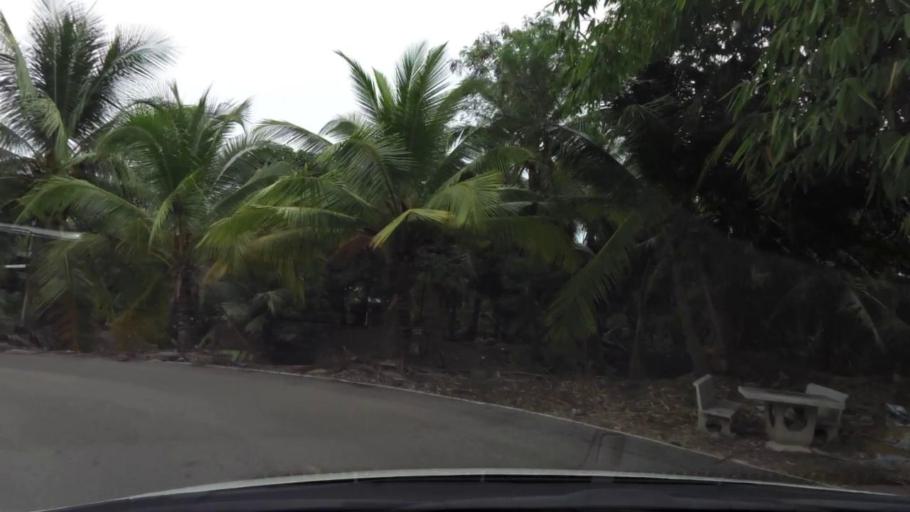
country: TH
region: Ratchaburi
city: Damnoen Saduak
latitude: 13.5679
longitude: 100.0212
